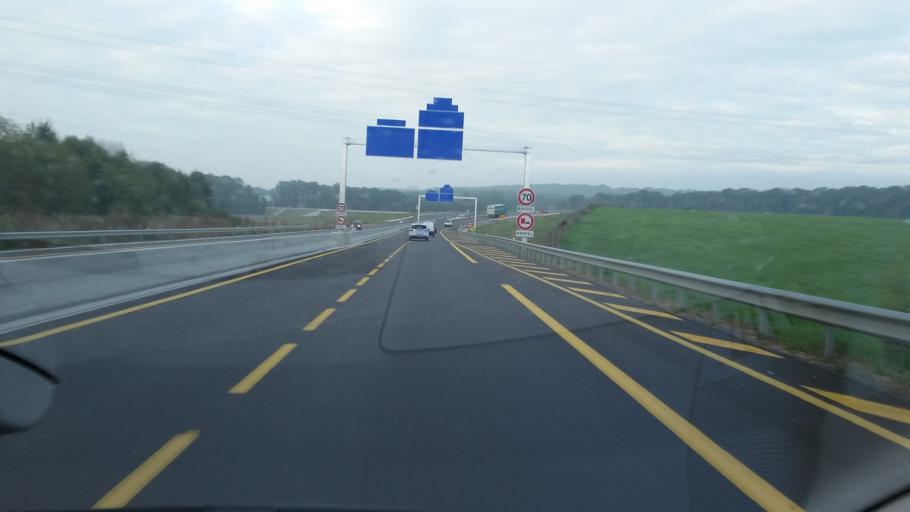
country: FR
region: Champagne-Ardenne
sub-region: Departement des Ardennes
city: La Francheville
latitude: 49.7224
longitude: 4.7064
